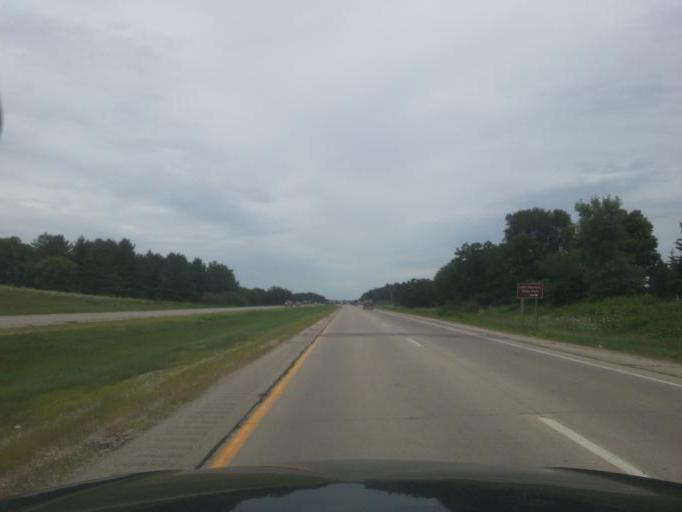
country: US
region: Wisconsin
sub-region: Dane County
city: McFarland
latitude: 43.0419
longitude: -89.2528
